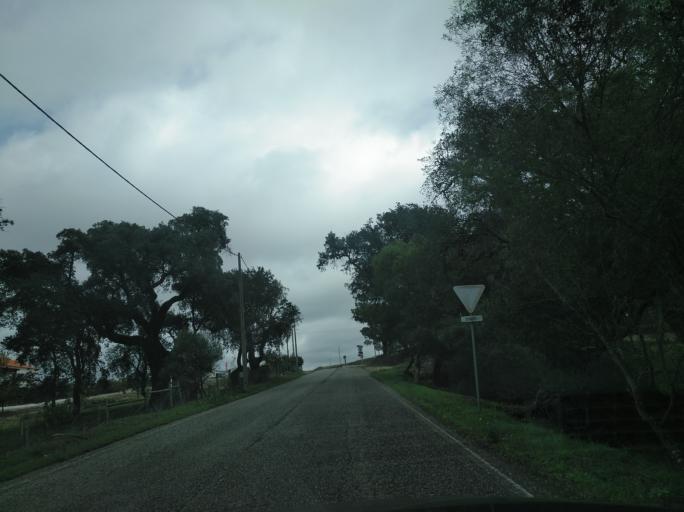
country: PT
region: Setubal
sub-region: Santiago do Cacem
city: Santo Andre
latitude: 38.1392
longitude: -8.7440
